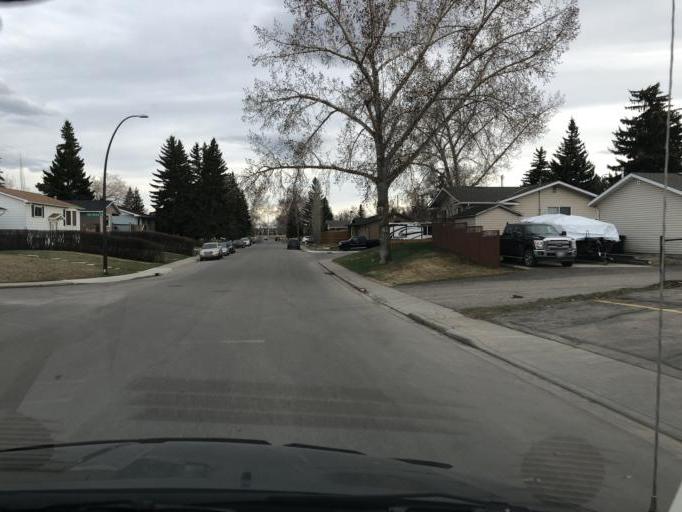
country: CA
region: Alberta
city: Calgary
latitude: 50.9420
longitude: -114.0336
